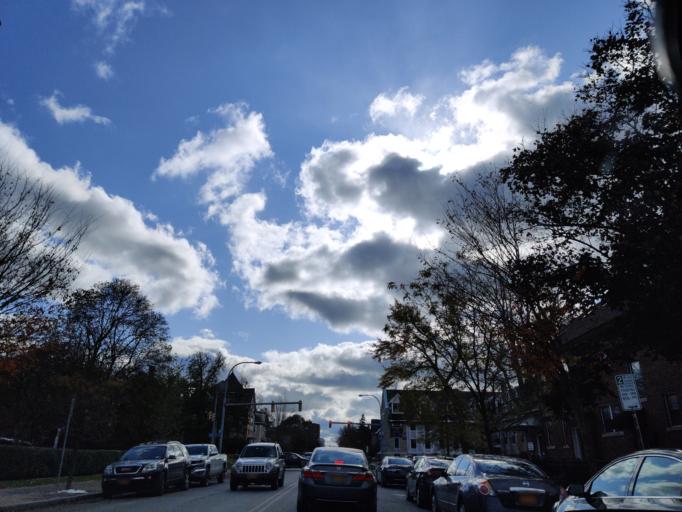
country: US
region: New York
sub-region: Erie County
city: Buffalo
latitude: 42.9160
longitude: -78.8771
